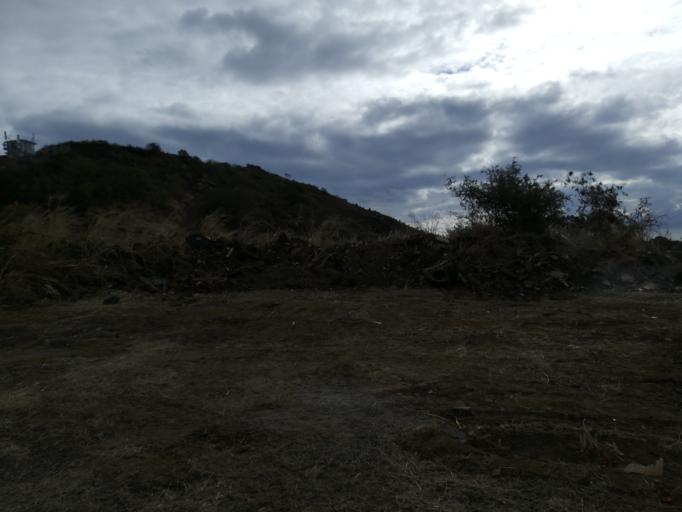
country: MU
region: Black River
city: Gros Cailloux
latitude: -20.2274
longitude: 57.4518
